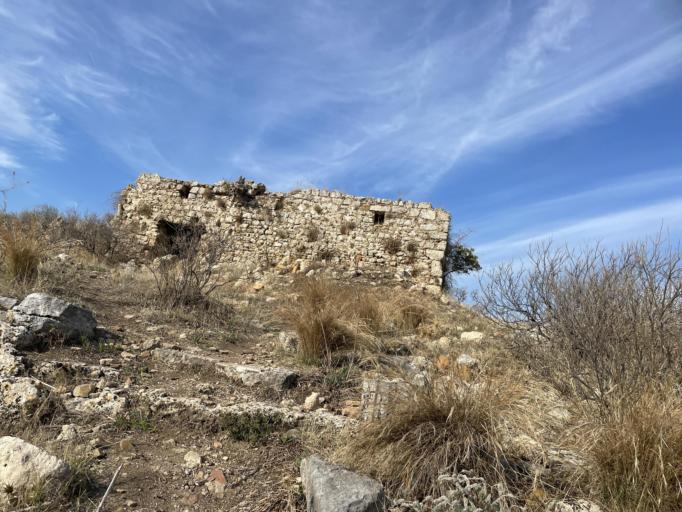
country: TR
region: Antalya
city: Aksu
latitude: 36.9675
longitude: 30.8560
